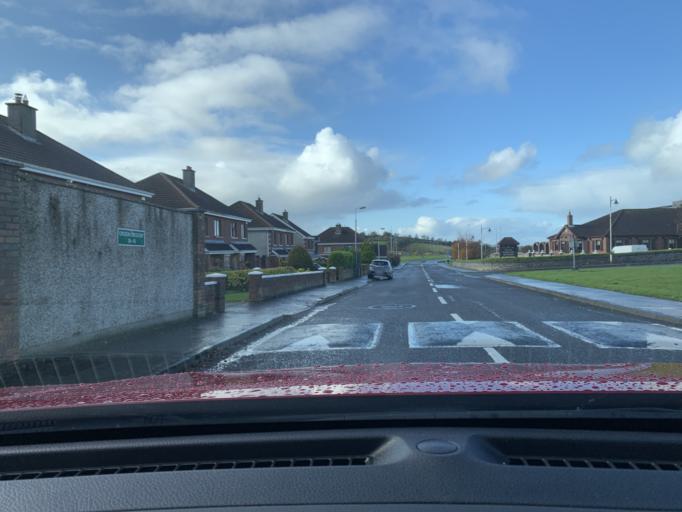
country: IE
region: Connaught
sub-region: Sligo
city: Sligo
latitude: 54.2614
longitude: -8.4730
